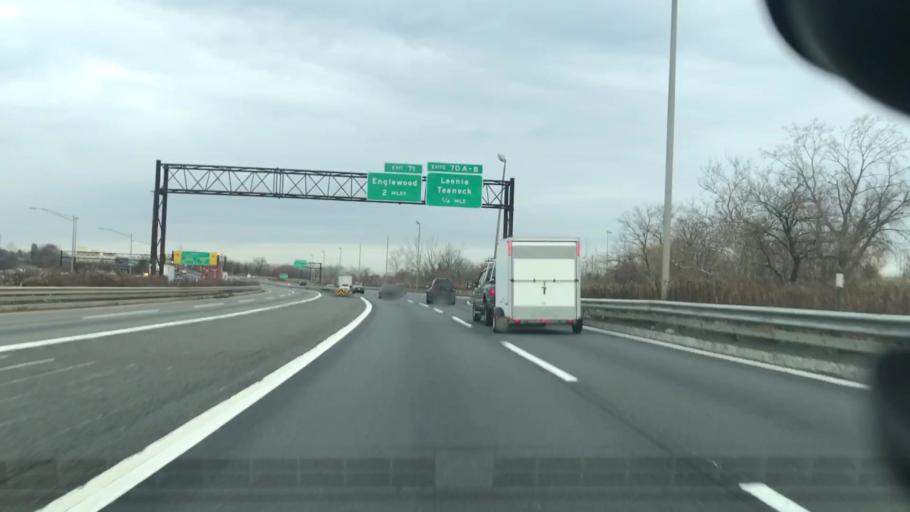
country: US
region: New Jersey
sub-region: Bergen County
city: Ridgefield Park
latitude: 40.8587
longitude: -74.0116
